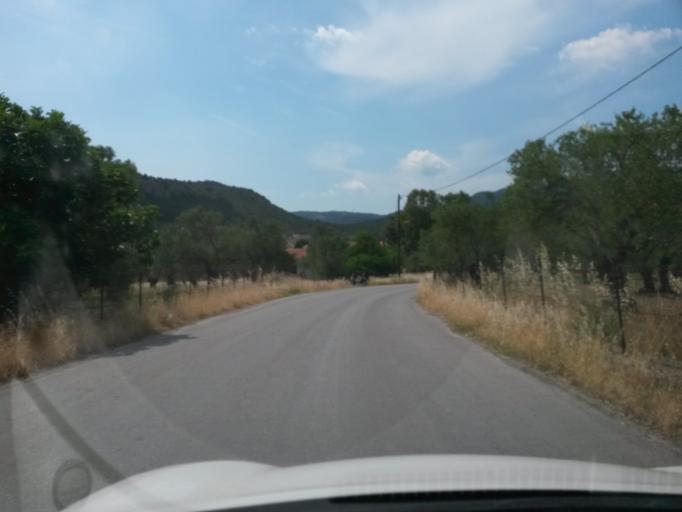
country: GR
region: North Aegean
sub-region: Nomos Lesvou
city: Kalloni
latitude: 39.2408
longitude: 26.2037
